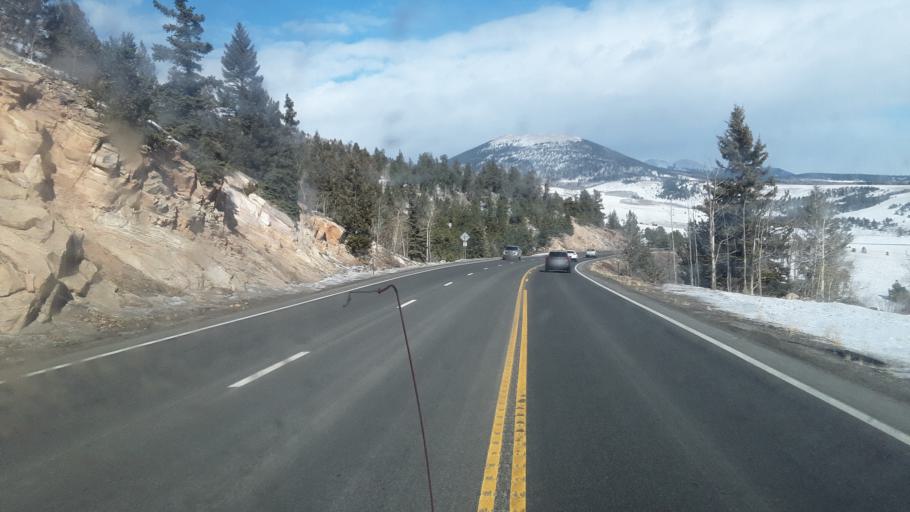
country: US
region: Colorado
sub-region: Park County
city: Fairplay
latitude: 39.2658
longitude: -105.9570
